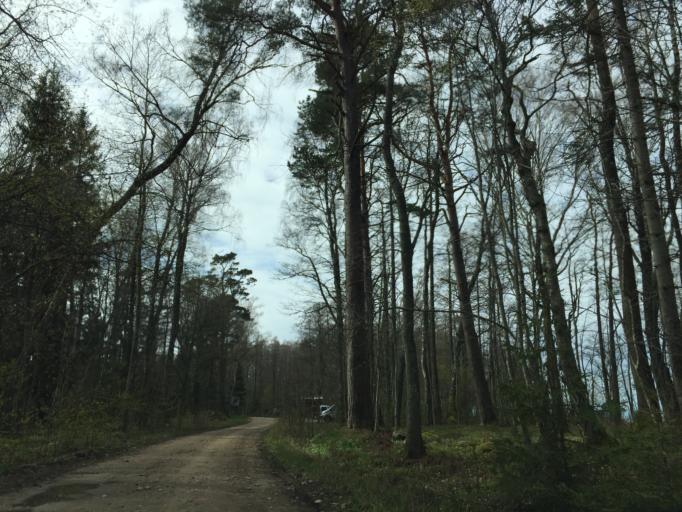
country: LV
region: Salacgrivas
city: Salacgriva
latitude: 57.5828
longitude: 24.3690
